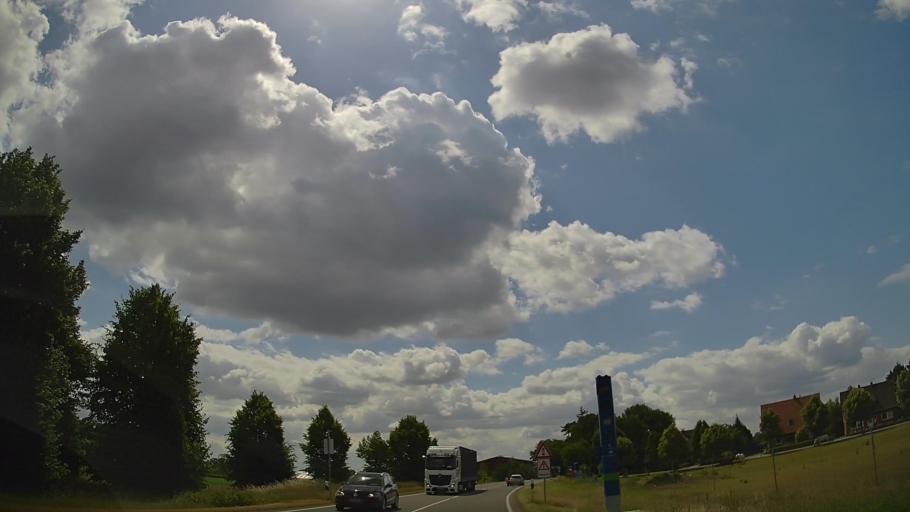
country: DE
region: Lower Saxony
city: Vechta
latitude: 52.7003
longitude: 8.3004
